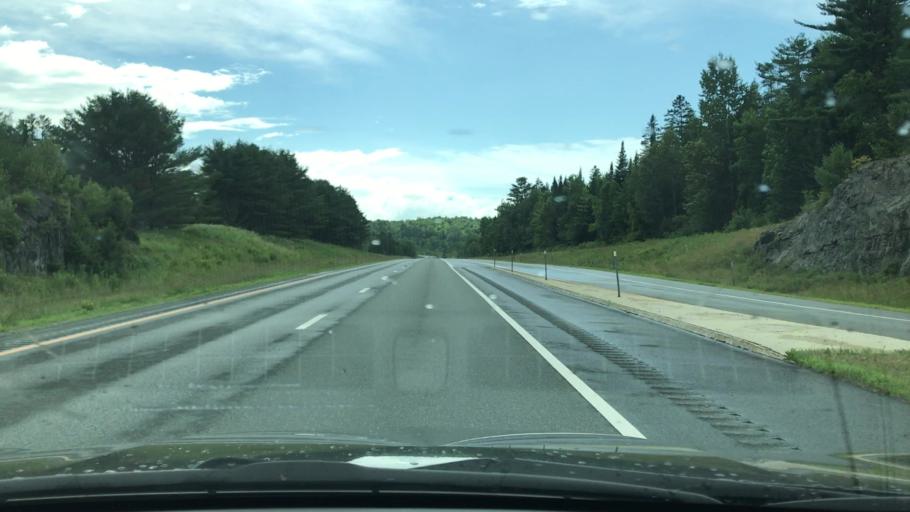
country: US
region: New Hampshire
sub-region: Grafton County
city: Littleton
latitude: 44.3247
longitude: -71.8101
